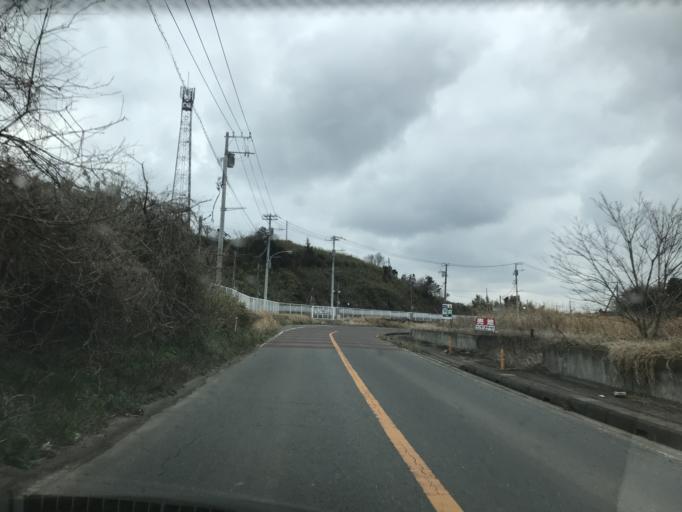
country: JP
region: Chiba
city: Sawara
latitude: 35.8348
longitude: 140.5038
